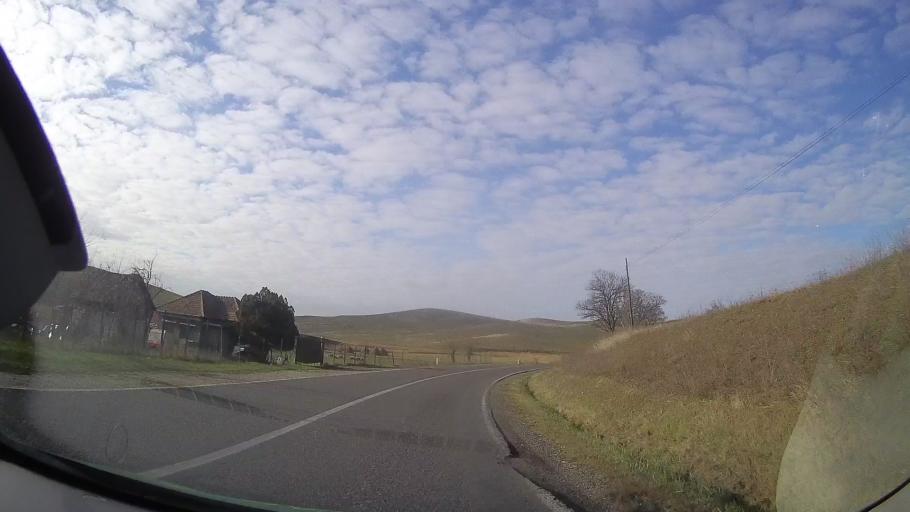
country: RO
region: Cluj
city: Jucu Herghelia
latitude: 46.8117
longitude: 23.8178
